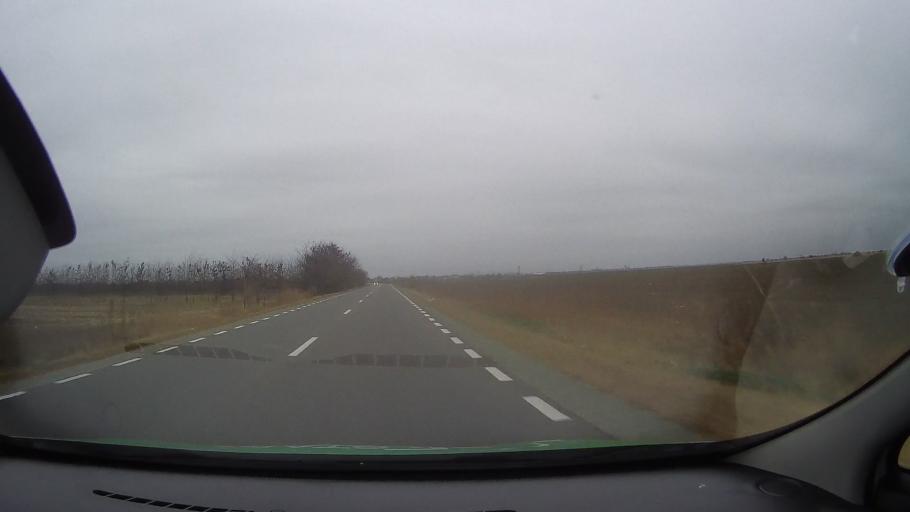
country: RO
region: Ialomita
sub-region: Comuna Slobozia
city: Slobozia
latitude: 44.6129
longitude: 27.3858
